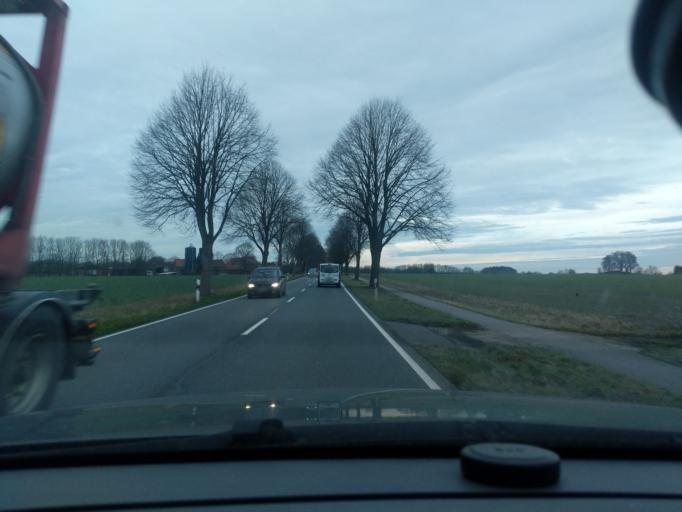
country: DE
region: Lower Saxony
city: Beckdorf
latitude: 53.4001
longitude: 9.6102
